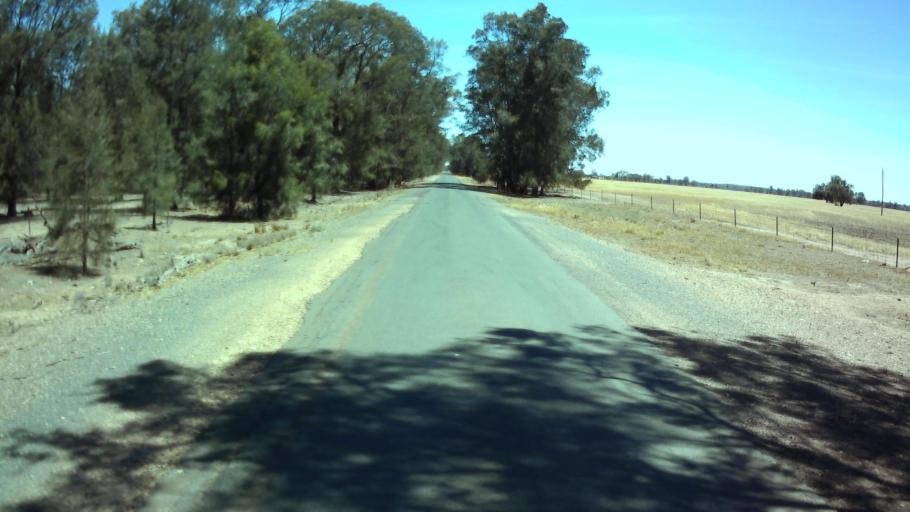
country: AU
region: New South Wales
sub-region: Weddin
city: Grenfell
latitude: -33.8800
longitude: 147.6902
